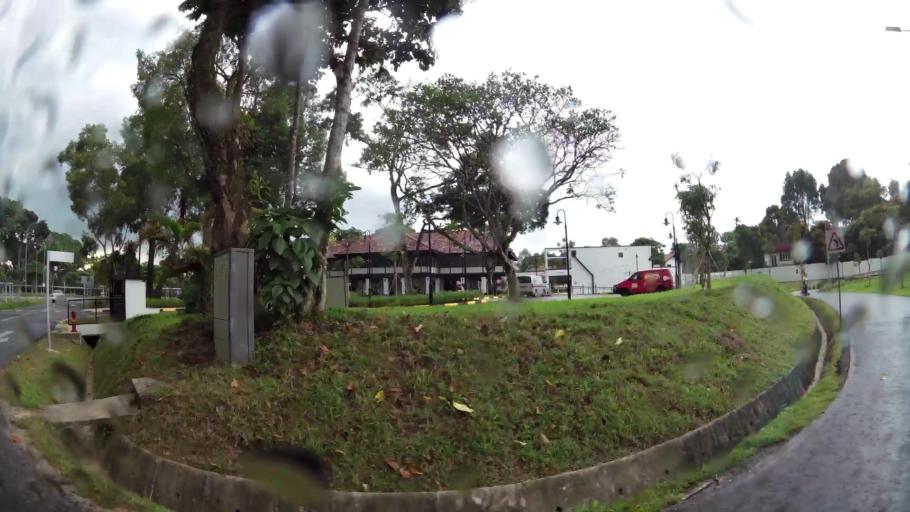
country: MY
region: Johor
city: Kampung Pasir Gudang Baru
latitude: 1.4085
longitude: 103.8686
